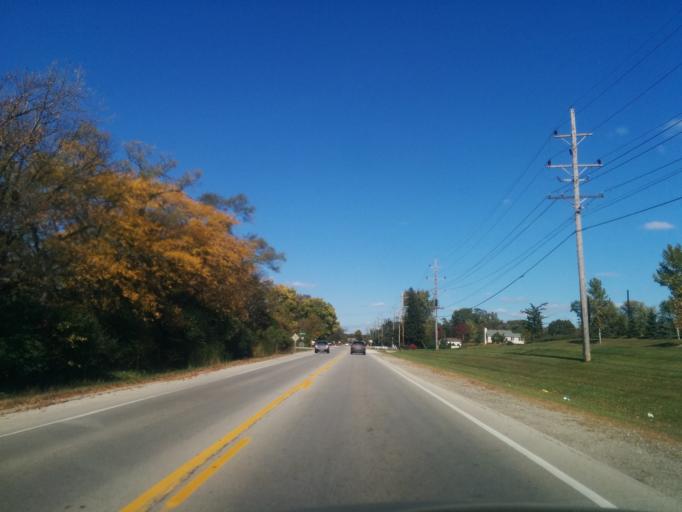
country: US
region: Illinois
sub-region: DuPage County
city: Lombard
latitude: 41.8688
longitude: -88.0331
